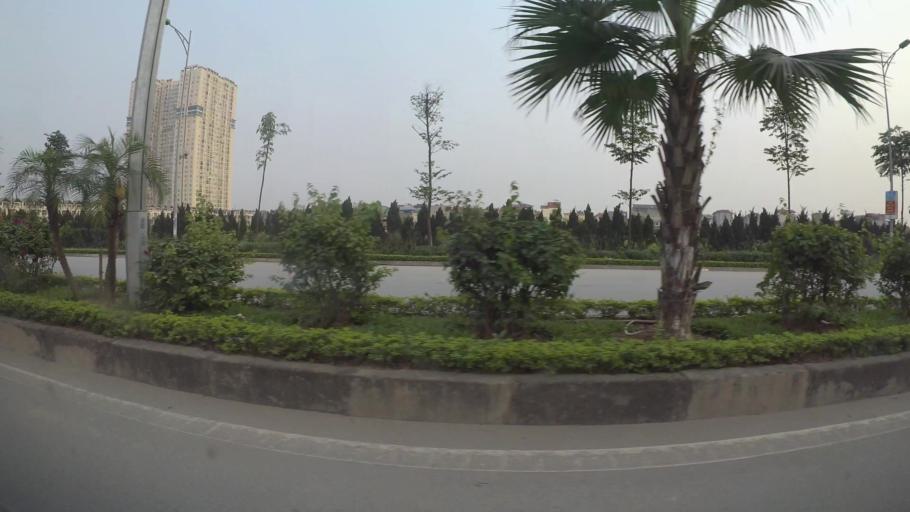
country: VN
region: Ha Noi
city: Cau Dien
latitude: 21.0048
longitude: 105.7290
